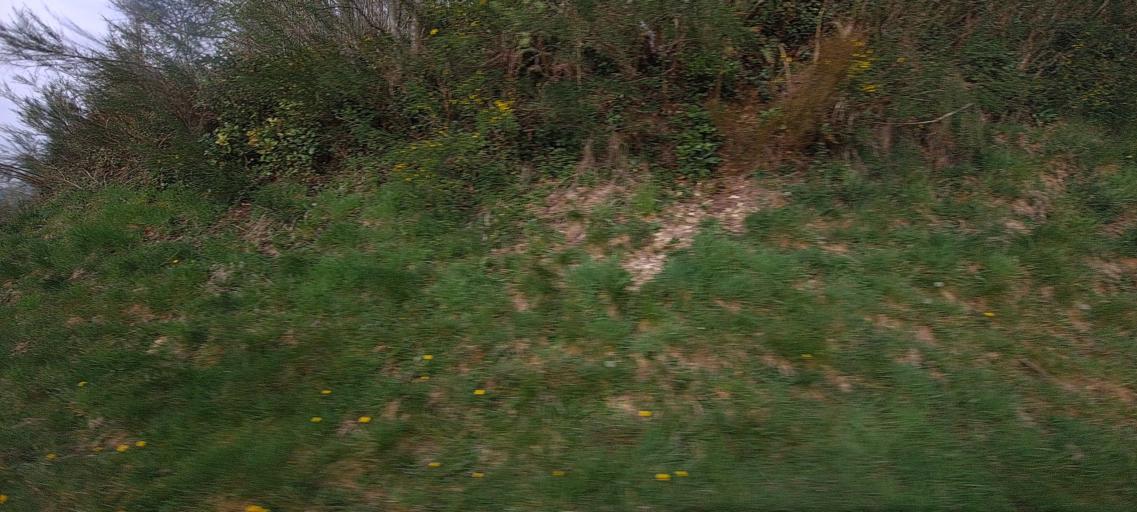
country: US
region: Oregon
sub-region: Clatsop County
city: Astoria
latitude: 46.1803
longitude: -123.8199
